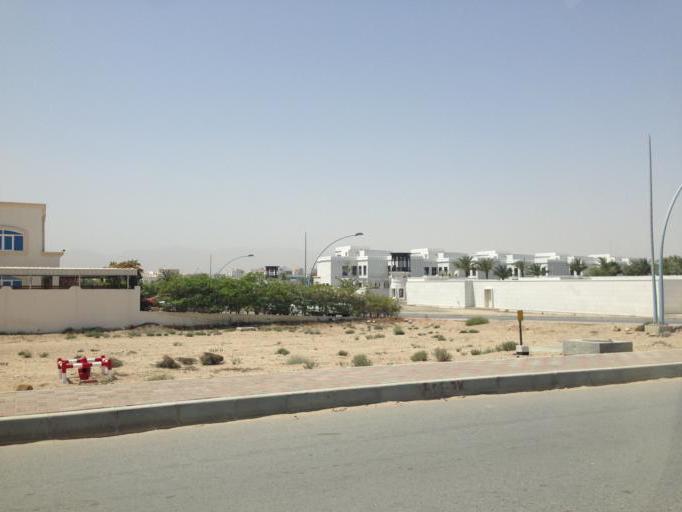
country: OM
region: Muhafazat Masqat
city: Bawshar
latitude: 23.6041
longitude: 58.3537
